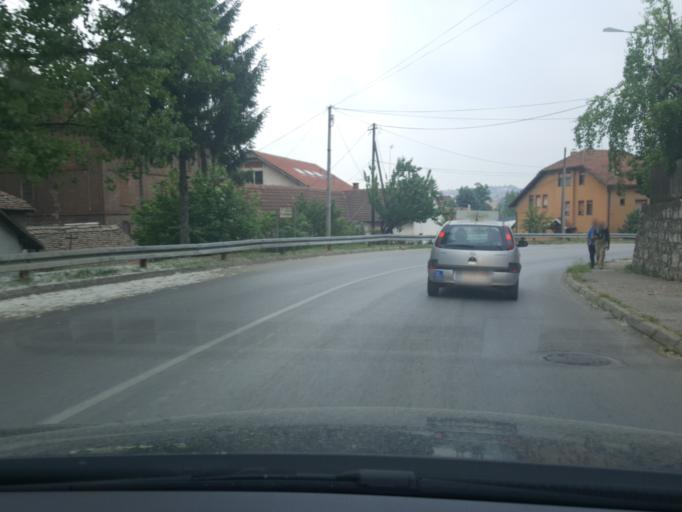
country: RS
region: Central Serbia
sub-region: Kolubarski Okrug
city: Valjevo
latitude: 44.2670
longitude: 19.8785
